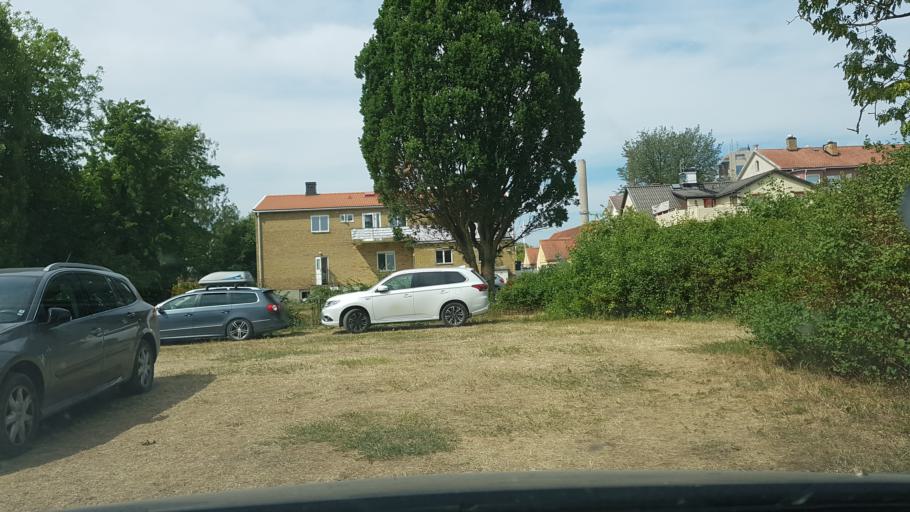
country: SE
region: Gotland
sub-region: Gotland
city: Slite
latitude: 57.7035
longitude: 18.8042
